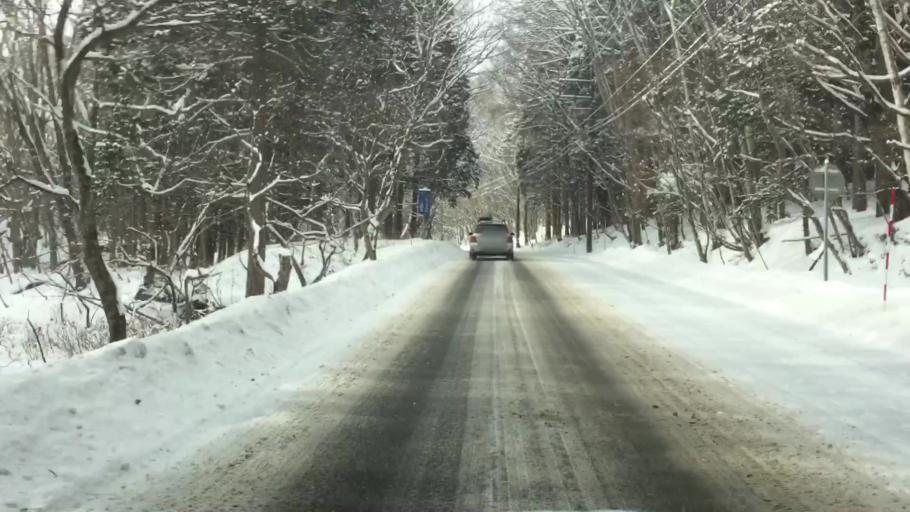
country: JP
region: Tochigi
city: Yaita
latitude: 36.9528
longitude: 139.7594
